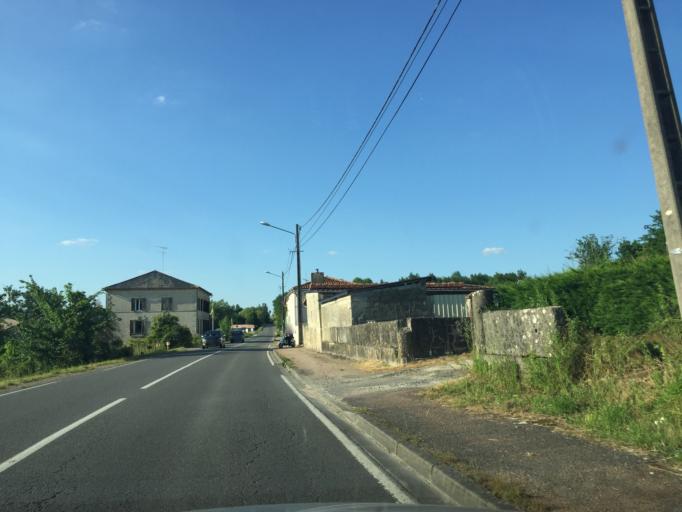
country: FR
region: Aquitaine
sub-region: Departement de la Dordogne
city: La Roche-Chalais
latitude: 45.1583
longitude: 0.0070
